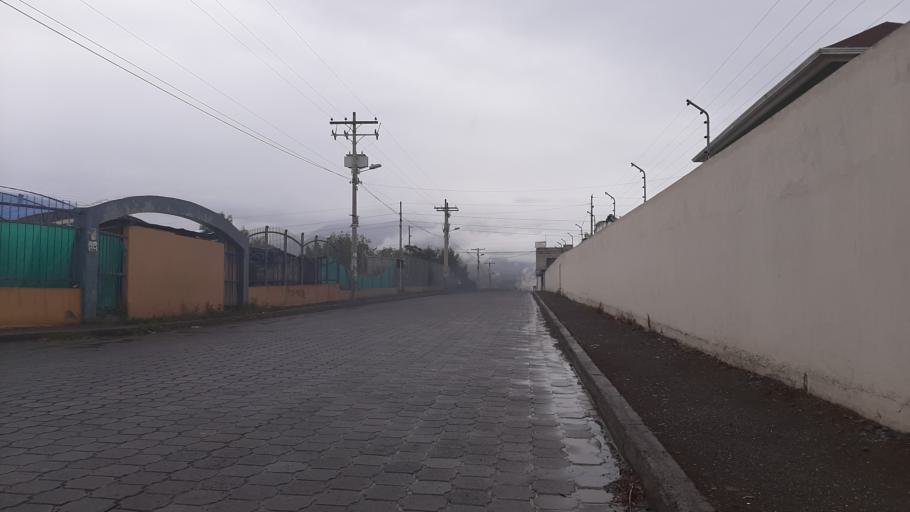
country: EC
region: Chimborazo
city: Riobamba
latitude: -1.6544
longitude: -78.6440
